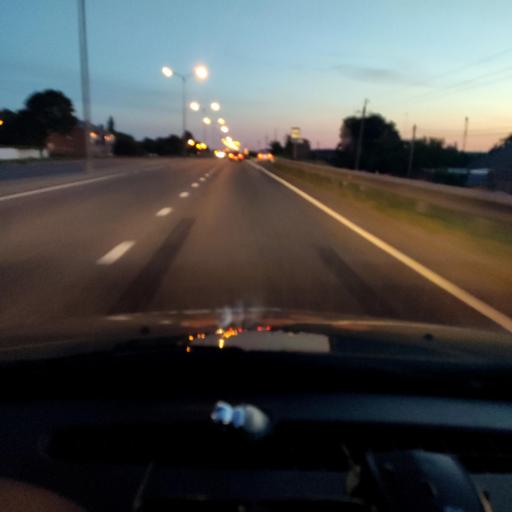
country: RU
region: Belgorod
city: Gubkin
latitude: 51.2629
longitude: 37.5425
